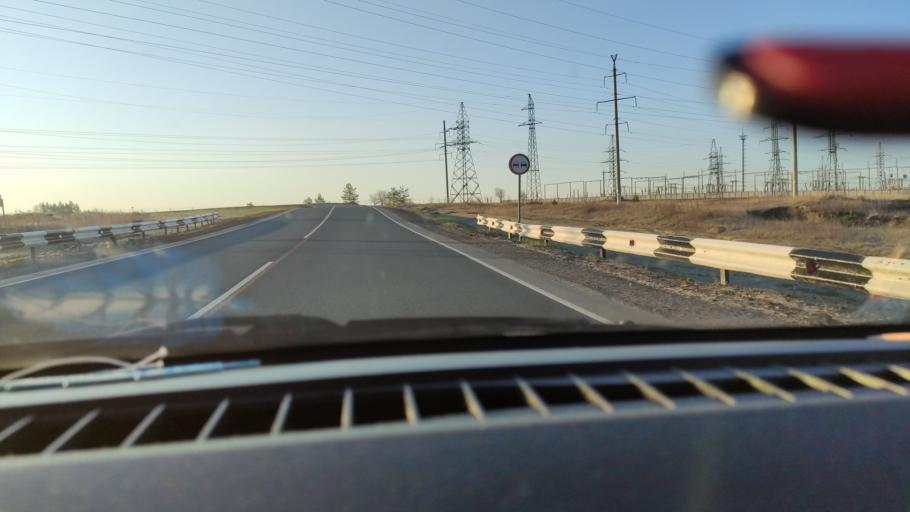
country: RU
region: Saratov
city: Sennoy
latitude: 52.1428
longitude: 46.9092
